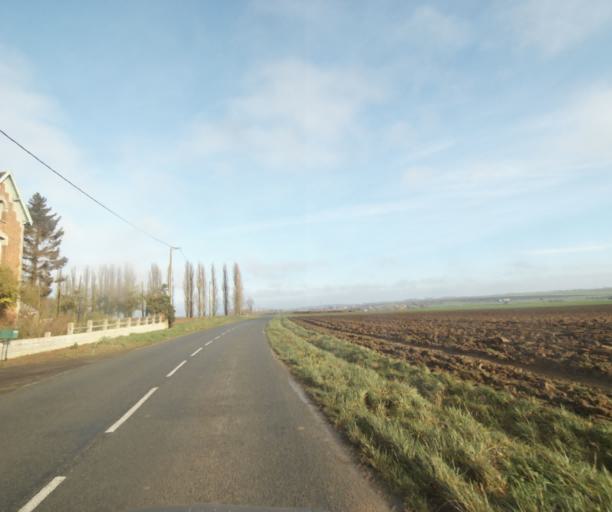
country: FR
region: Nord-Pas-de-Calais
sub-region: Departement du Nord
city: Haspres
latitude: 50.2766
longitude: 3.4369
